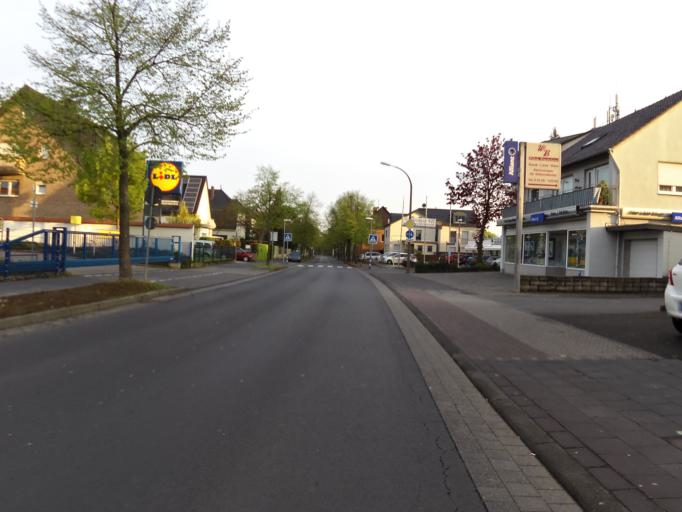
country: DE
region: North Rhine-Westphalia
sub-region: Regierungsbezirk Koln
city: Rheinbach
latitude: 50.6296
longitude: 6.9439
